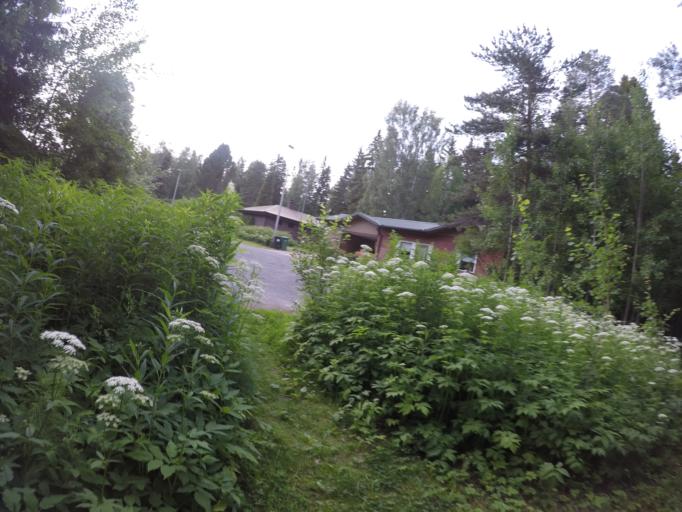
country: FI
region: Haeme
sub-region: Haemeenlinna
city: Haemeenlinna
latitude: 60.9745
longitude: 24.3986
